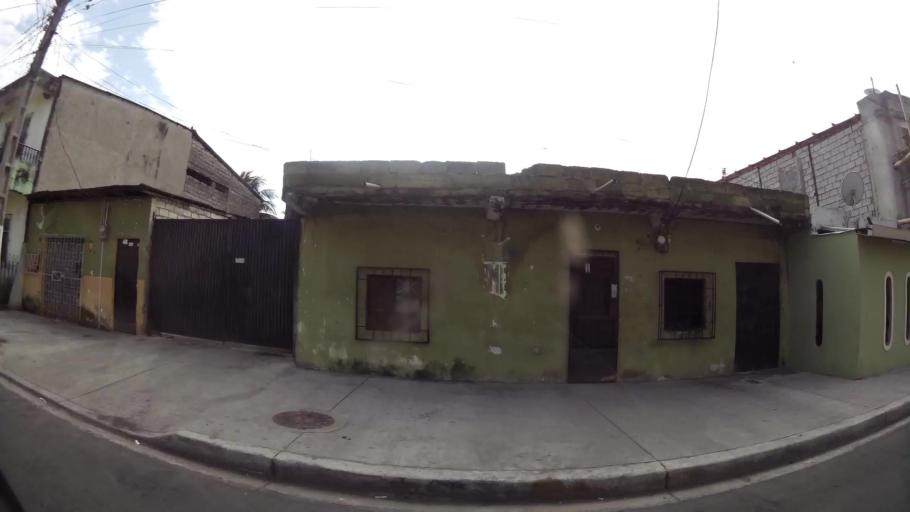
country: EC
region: Guayas
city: Guayaquil
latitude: -2.2500
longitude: -79.8804
